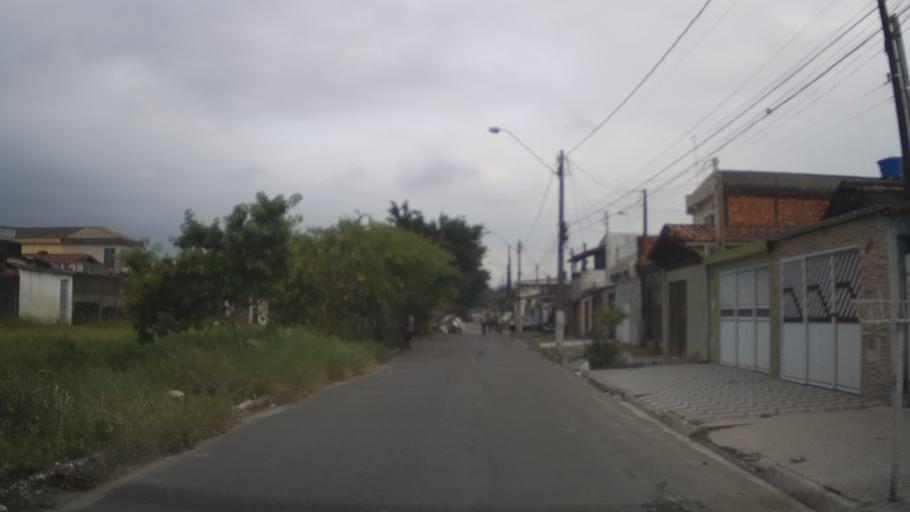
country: BR
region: Sao Paulo
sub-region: Praia Grande
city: Praia Grande
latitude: -24.0034
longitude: -46.4449
